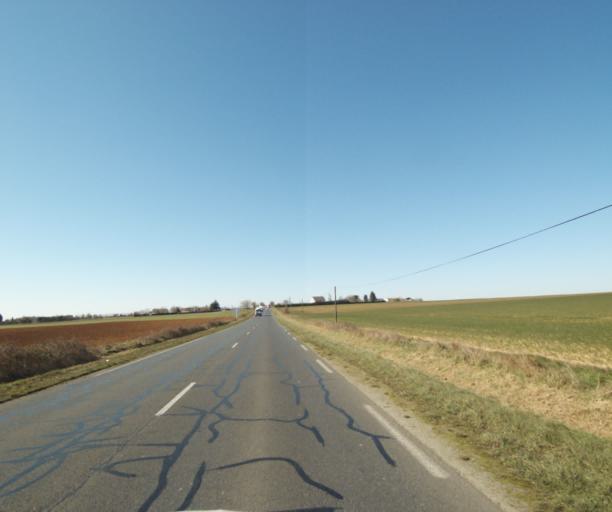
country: FR
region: Poitou-Charentes
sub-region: Departement des Deux-Sevres
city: Magne
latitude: 46.3511
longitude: -0.5188
